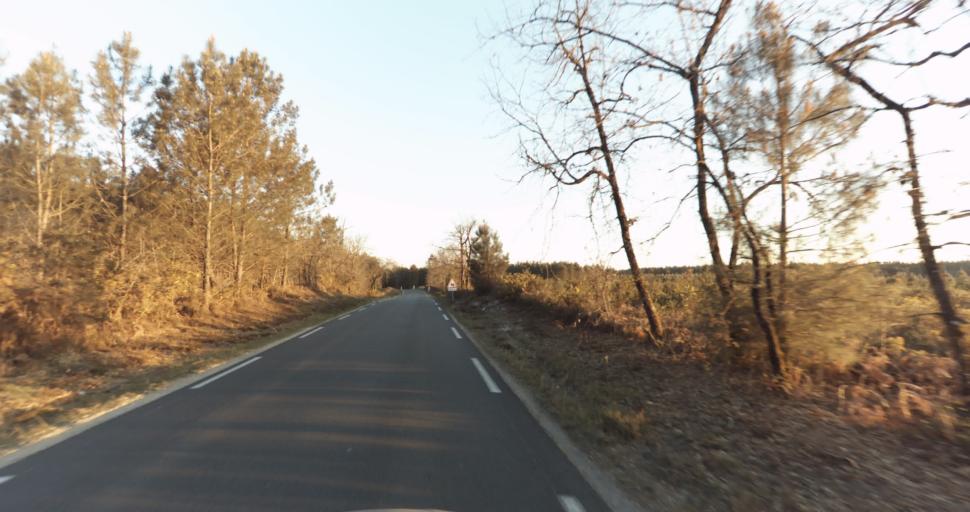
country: FR
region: Aquitaine
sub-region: Departement de la Gironde
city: Martignas-sur-Jalle
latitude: 44.8241
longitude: -0.7581
